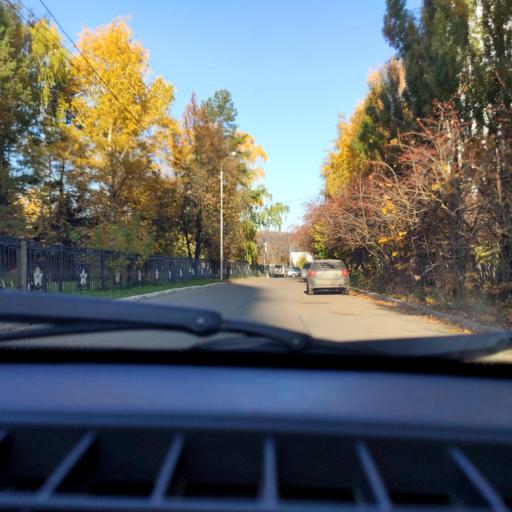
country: RU
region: Bashkortostan
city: Ufa
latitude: 54.7700
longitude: 56.0102
